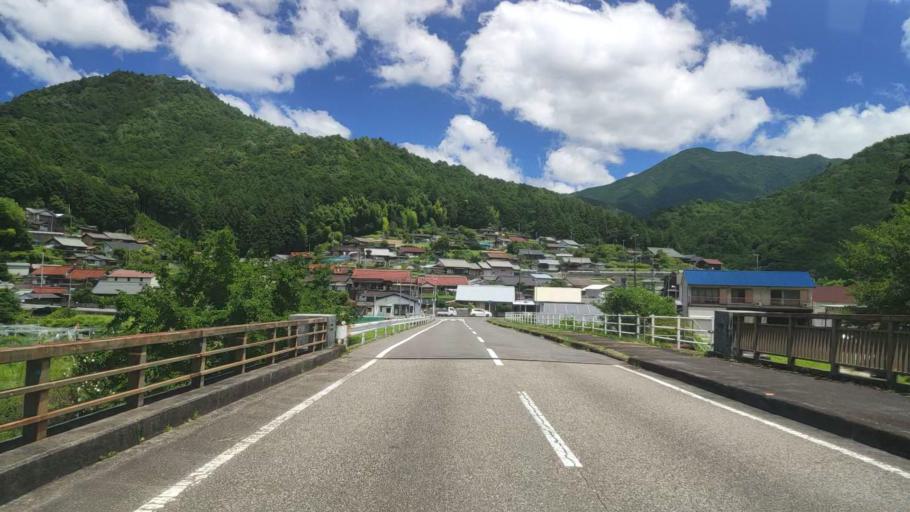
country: JP
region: Mie
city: Owase
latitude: 33.9833
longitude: 136.0398
